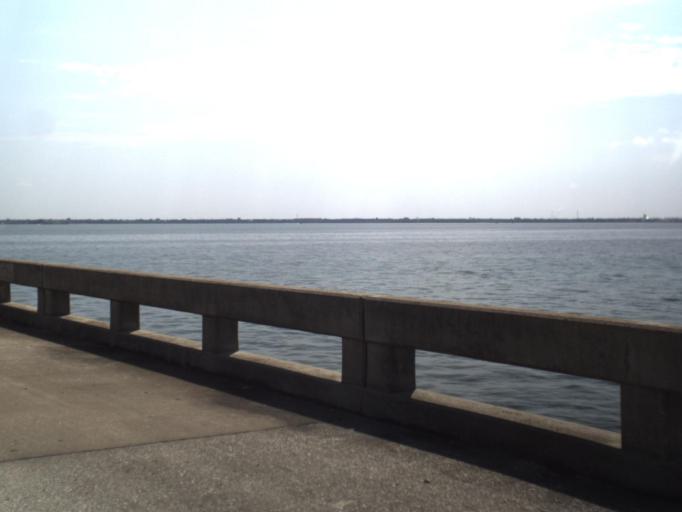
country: US
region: Florida
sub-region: Pinellas County
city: Gandy
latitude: 27.8824
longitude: -82.5710
